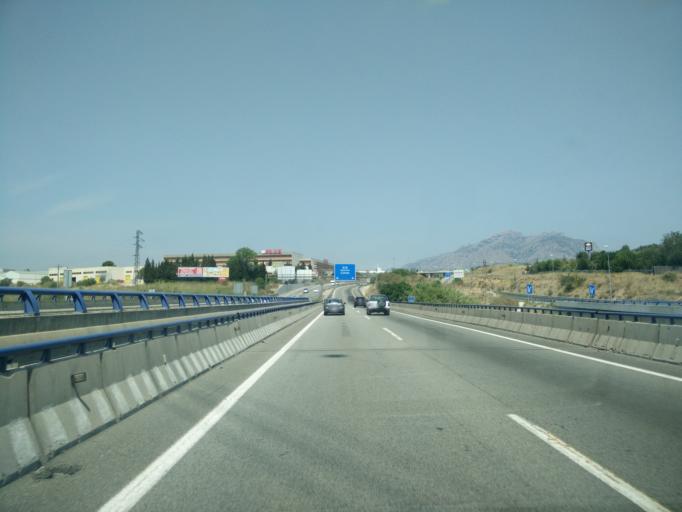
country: ES
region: Catalonia
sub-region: Provincia de Barcelona
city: Abrera
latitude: 41.5241
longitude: 1.8842
